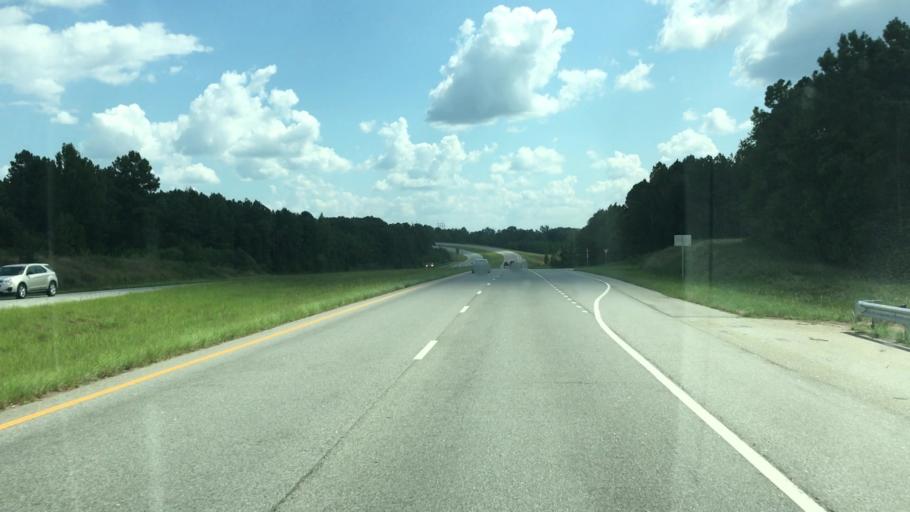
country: US
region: Georgia
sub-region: Putnam County
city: Eatonton
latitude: 33.2834
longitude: -83.3710
